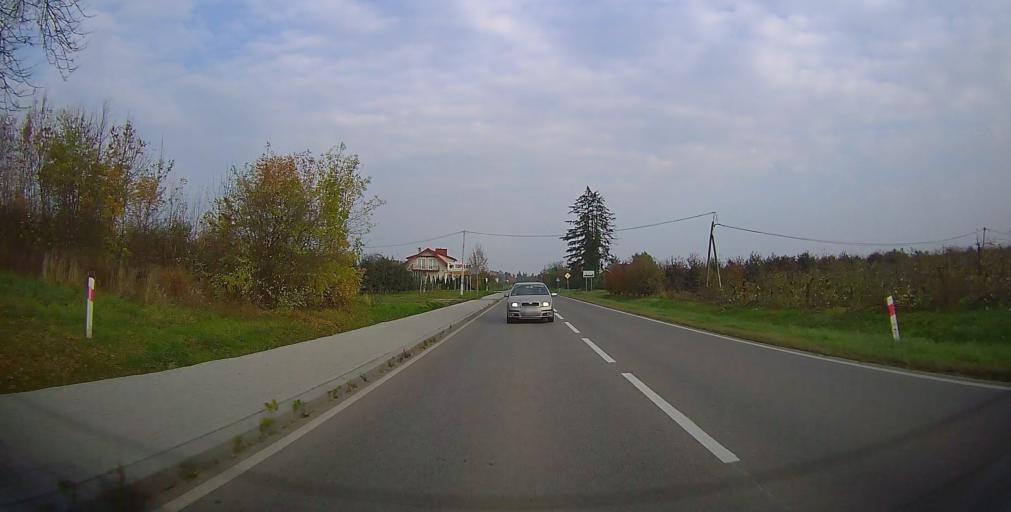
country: PL
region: Masovian Voivodeship
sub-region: Powiat grojecki
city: Belsk Duzy
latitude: 51.7711
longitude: 20.7690
